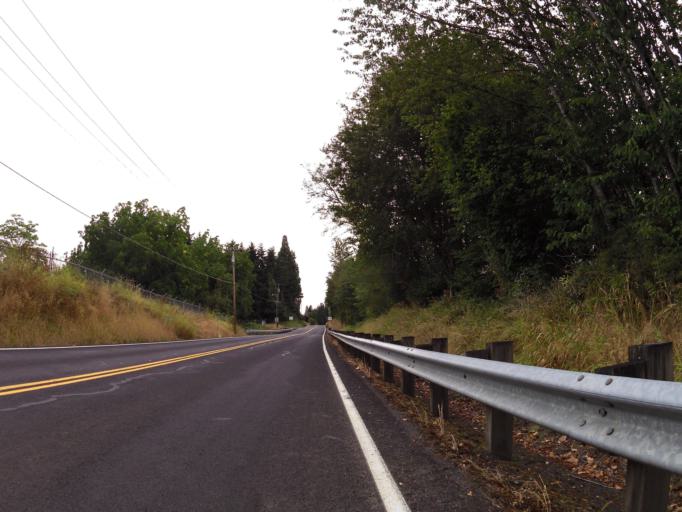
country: US
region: Washington
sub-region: Cowlitz County
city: Castle Rock
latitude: 46.2353
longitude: -122.8894
